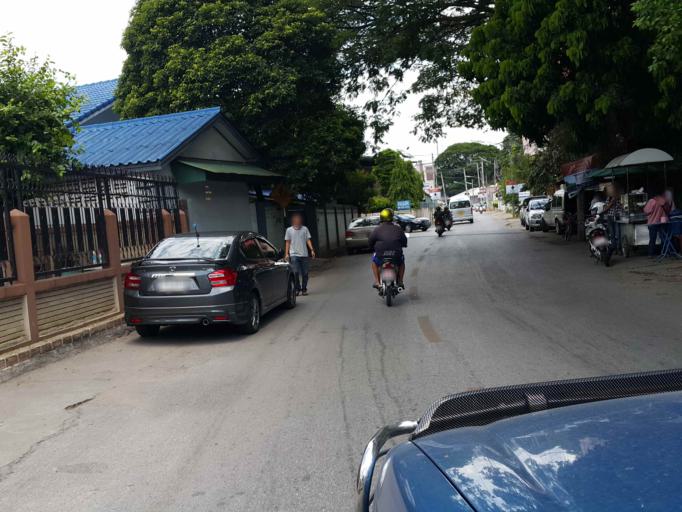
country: TH
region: Chiang Mai
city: Chiang Mai
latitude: 18.7836
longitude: 99.0131
